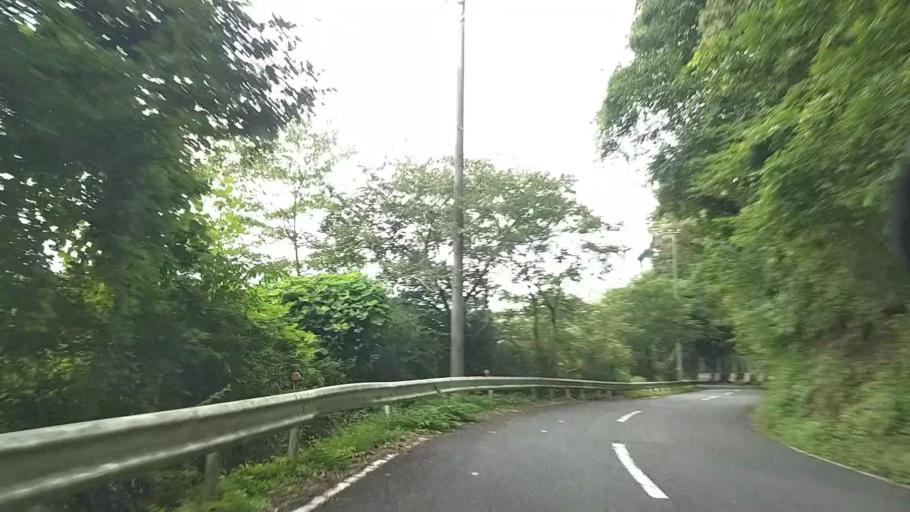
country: JP
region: Shizuoka
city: Fujinomiya
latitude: 35.2061
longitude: 138.5468
